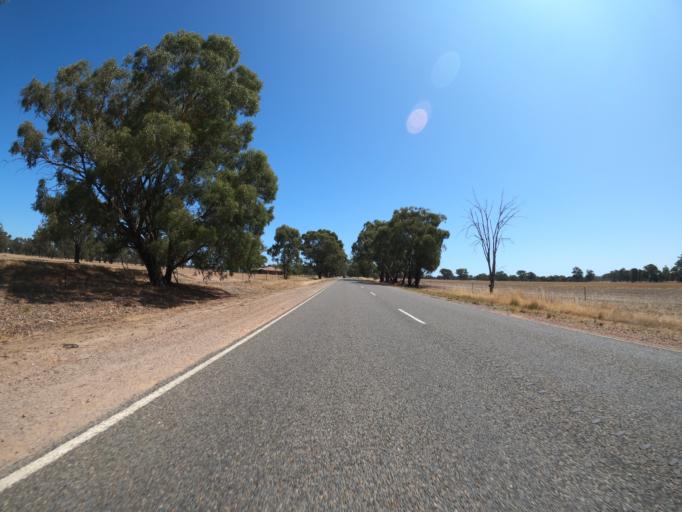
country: AU
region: New South Wales
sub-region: Corowa Shire
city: Corowa
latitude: -36.0679
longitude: 146.3603
